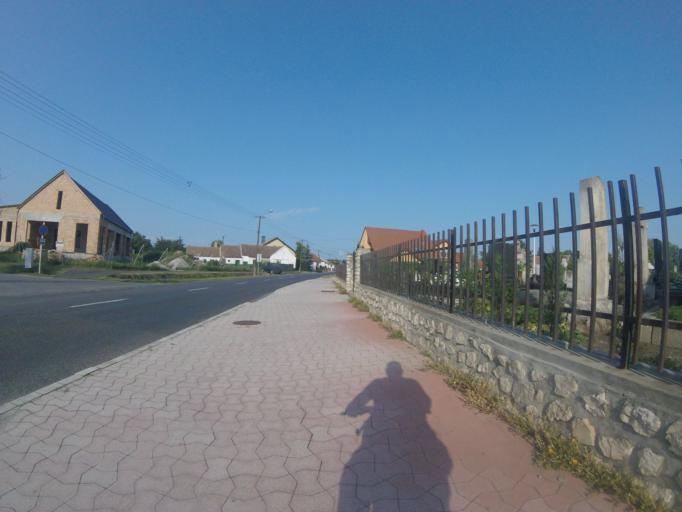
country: HU
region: Gyor-Moson-Sopron
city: Nagycenk
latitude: 47.6208
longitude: 16.7646
